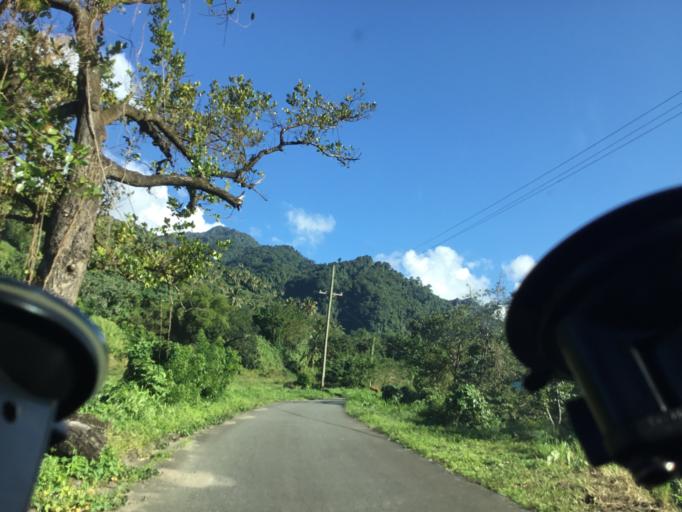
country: VC
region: Saint David
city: Chateaubelair
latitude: 13.3070
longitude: -61.2310
